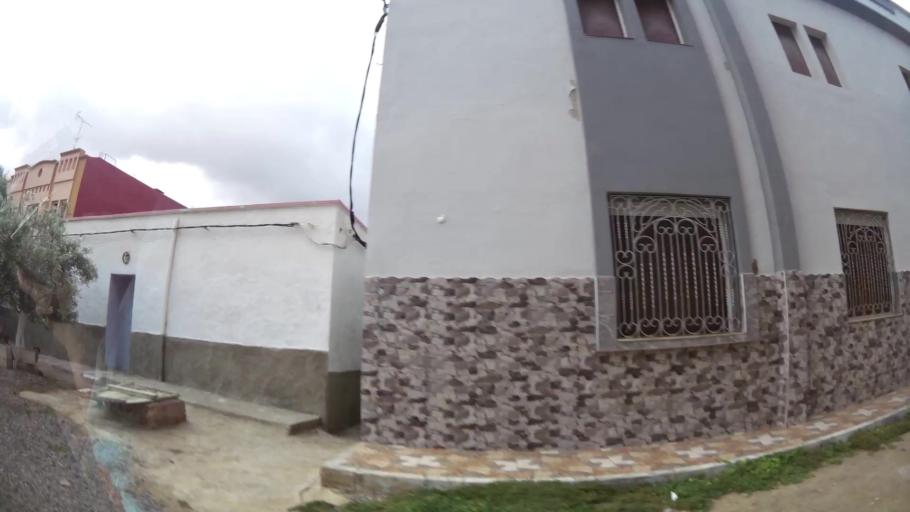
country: MA
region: Oriental
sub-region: Nador
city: Nador
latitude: 35.1555
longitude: -2.9143
